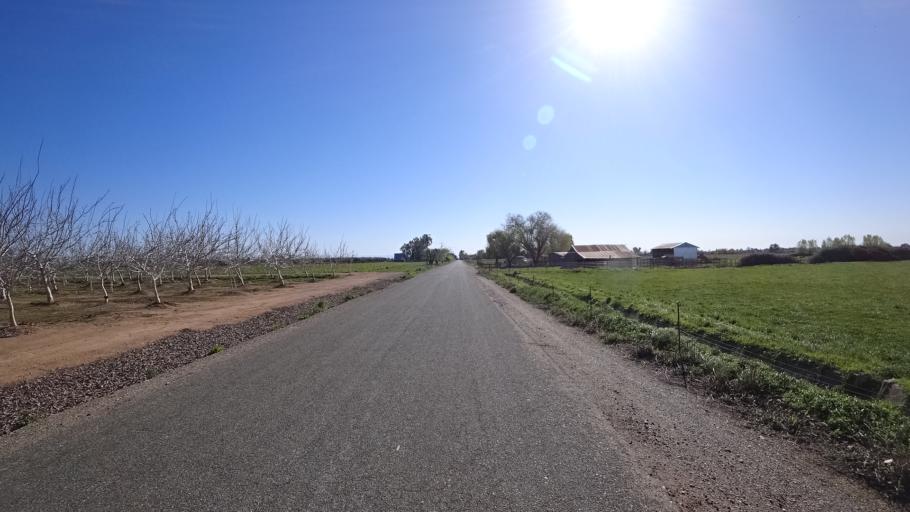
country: US
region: California
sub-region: Glenn County
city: Orland
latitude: 39.7370
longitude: -122.2352
